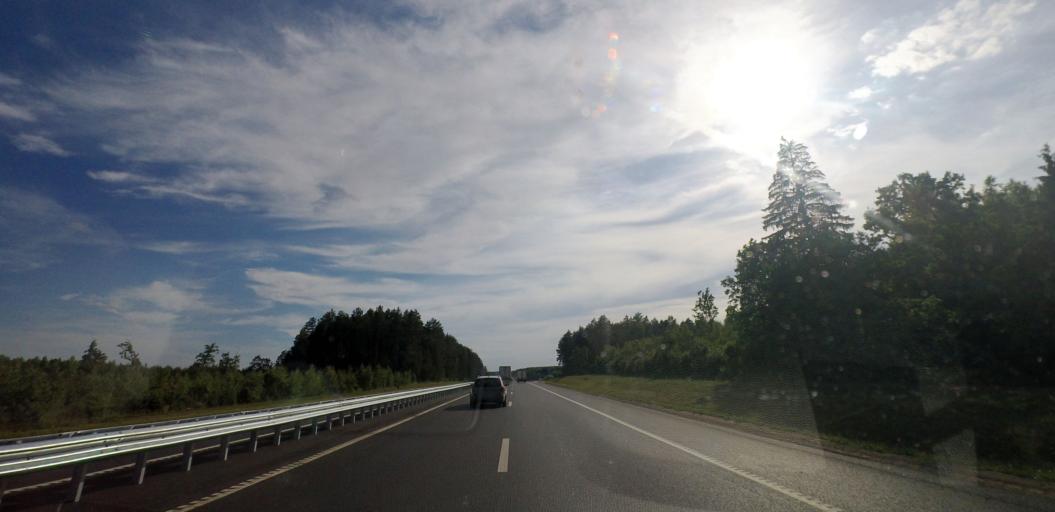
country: BY
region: Grodnenskaya
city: Lida
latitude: 53.8306
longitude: 25.1436
